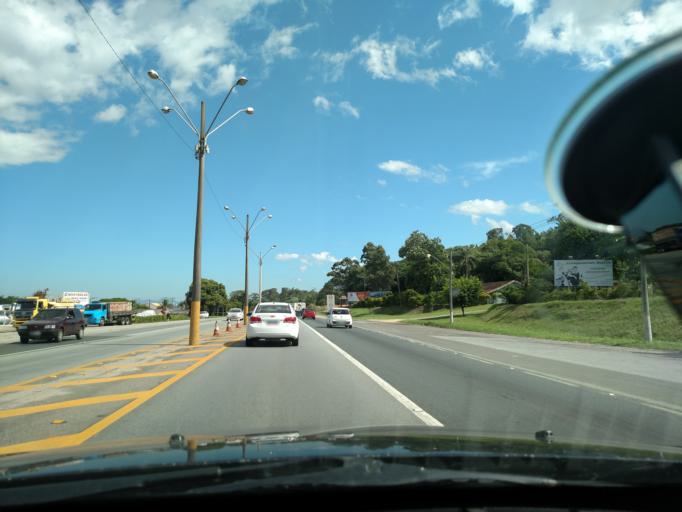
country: BR
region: Santa Catarina
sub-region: Biguacu
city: Biguacu
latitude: -27.4700
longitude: -48.6415
